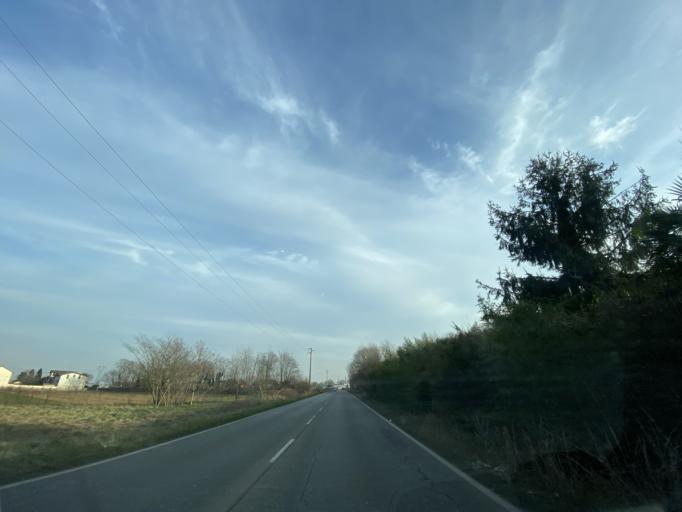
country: IT
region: Lombardy
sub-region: Citta metropolitana di Milano
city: Cernusco sul Naviglio
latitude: 45.5334
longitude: 9.3453
